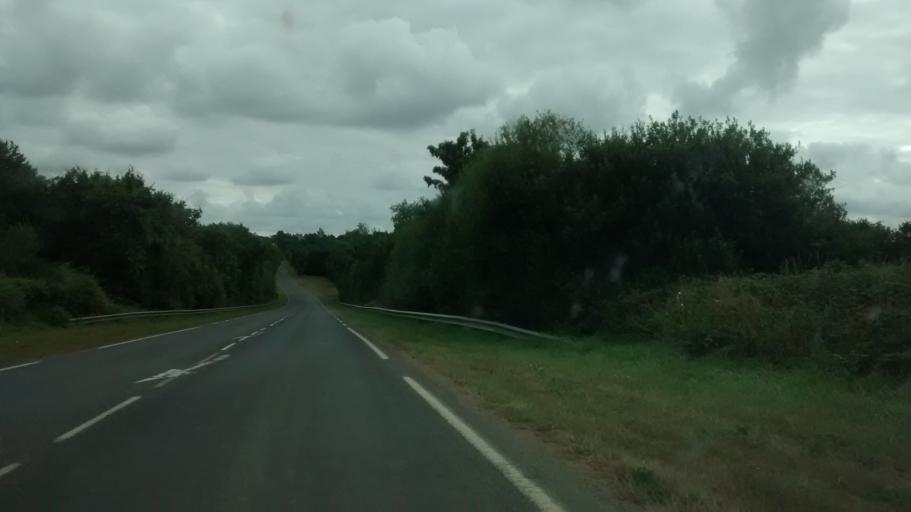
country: FR
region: Brittany
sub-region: Departement du Finistere
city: Le Folgoet
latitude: 48.5525
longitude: -4.3459
